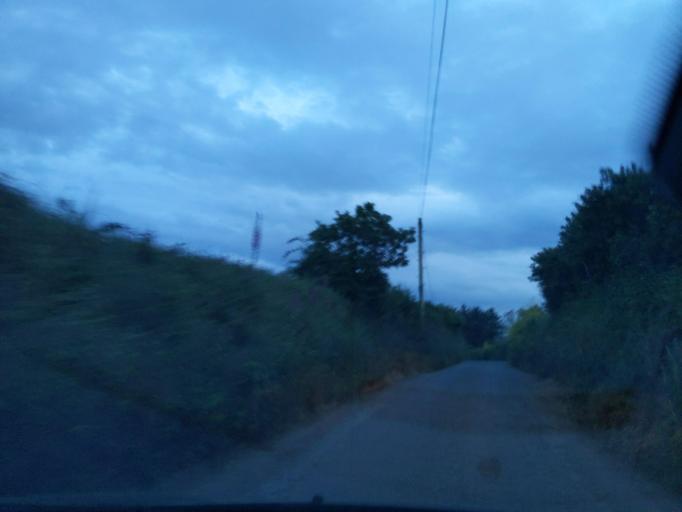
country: GB
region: England
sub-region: Cornwall
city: Wadebridge
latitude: 50.5753
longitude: -4.8295
